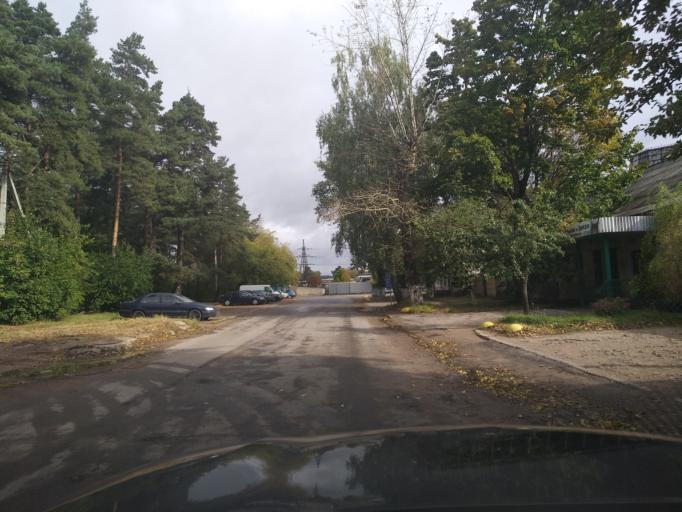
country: BY
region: Minsk
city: Minsk
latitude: 53.8782
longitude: 27.6410
